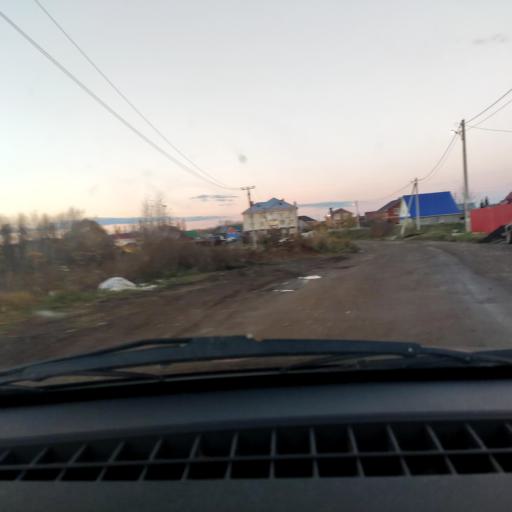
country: RU
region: Bashkortostan
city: Ufa
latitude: 54.6422
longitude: 55.9167
